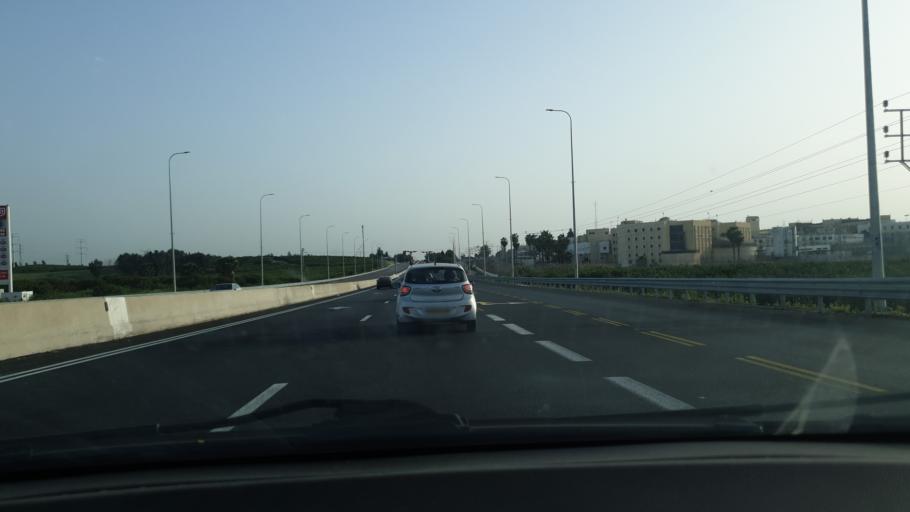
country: IL
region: Central District
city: Even Yehuda
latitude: 32.2441
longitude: 34.8879
